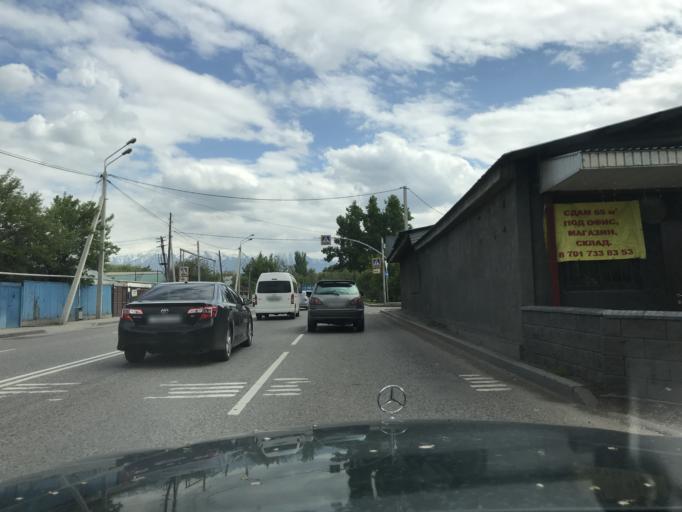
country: KZ
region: Almaty Qalasy
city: Almaty
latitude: 43.2926
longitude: 76.9003
